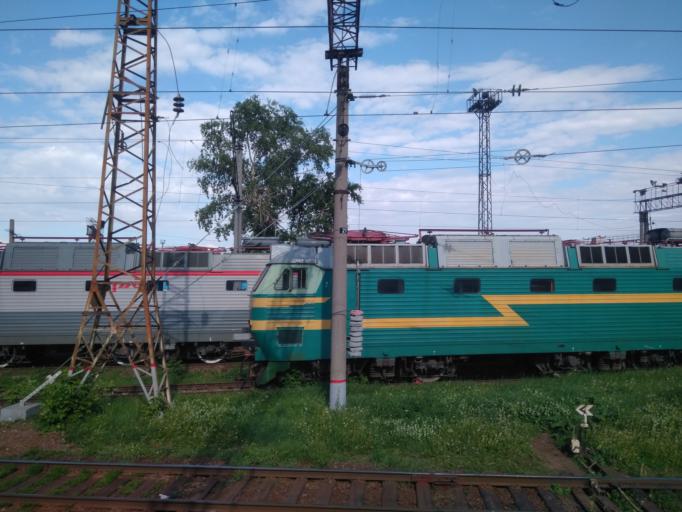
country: RU
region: Moscow
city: Mar'ina Roshcha
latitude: 55.7901
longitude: 37.6422
